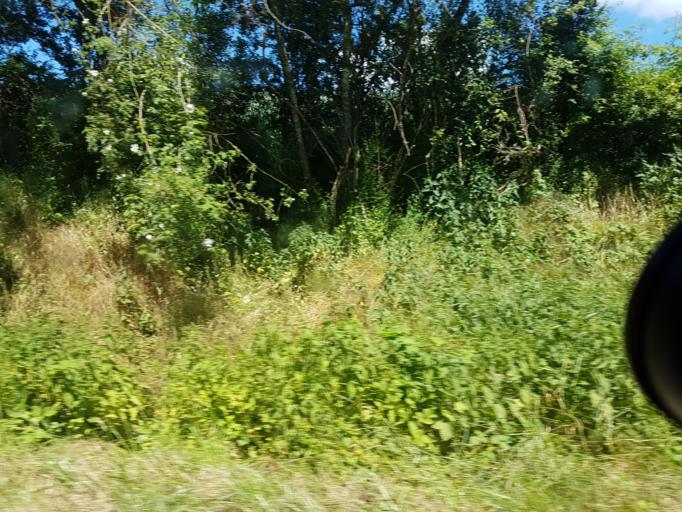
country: FR
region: Bourgogne
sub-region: Departement de Saone-et-Loire
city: Autun
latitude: 47.0565
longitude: 4.2762
